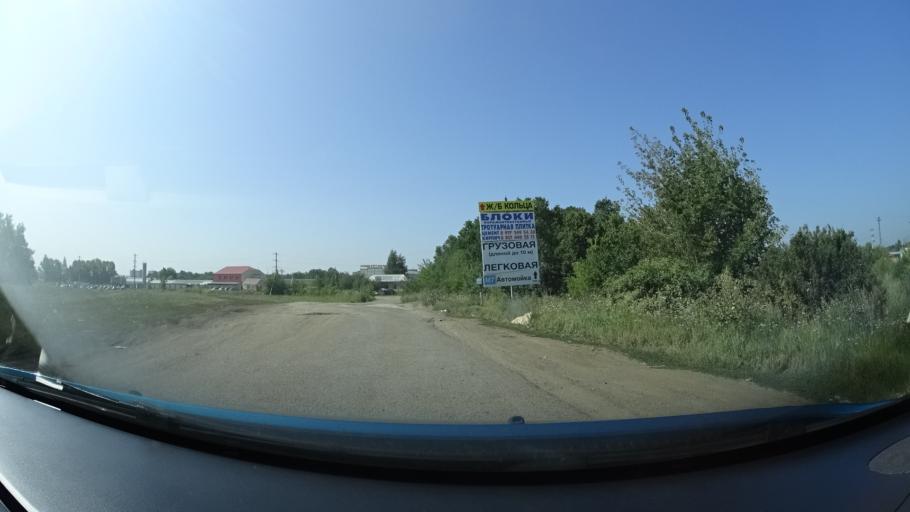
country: RU
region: Bashkortostan
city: Mikhaylovka
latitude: 54.8064
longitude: 55.8507
